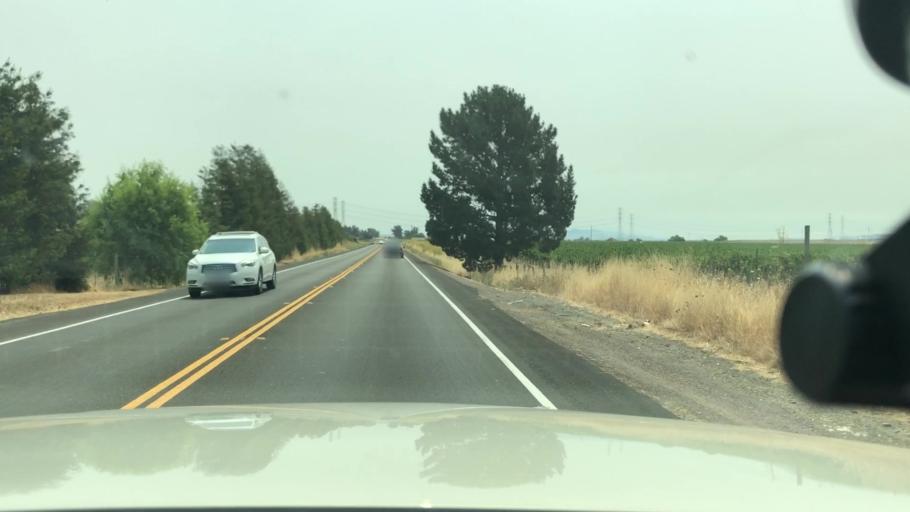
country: US
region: California
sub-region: Marin County
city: Black Point-Green Point
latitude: 38.1673
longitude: -122.5137
